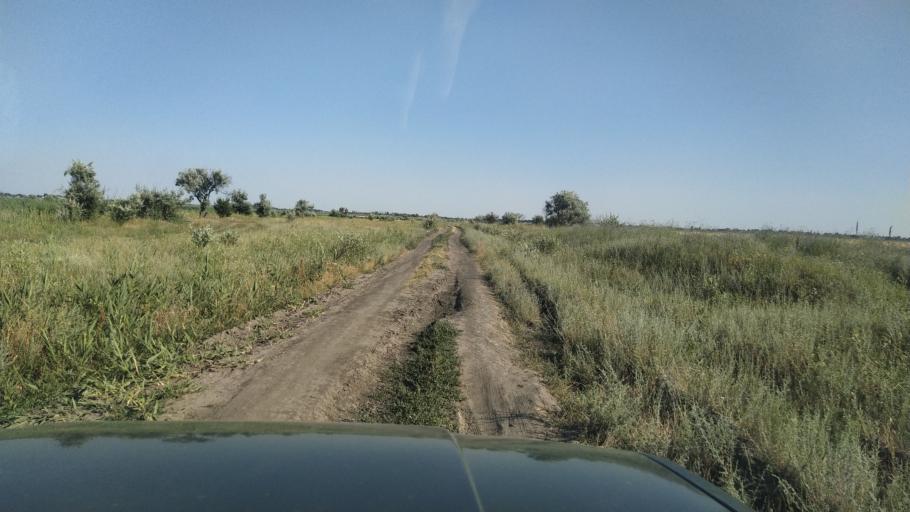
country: RU
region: Rostov
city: Kuleshovka
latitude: 47.1304
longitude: 39.6438
